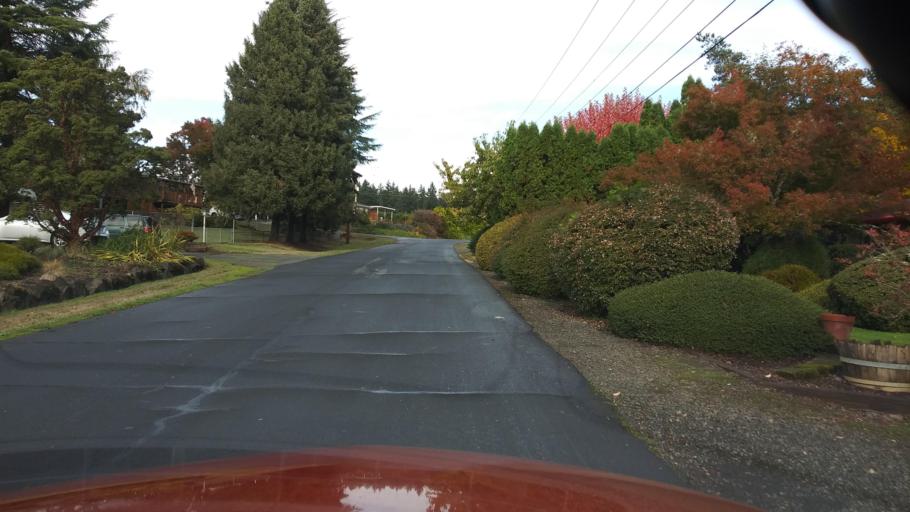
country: US
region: Oregon
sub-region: Washington County
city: Forest Grove
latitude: 45.5319
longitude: -123.1348
